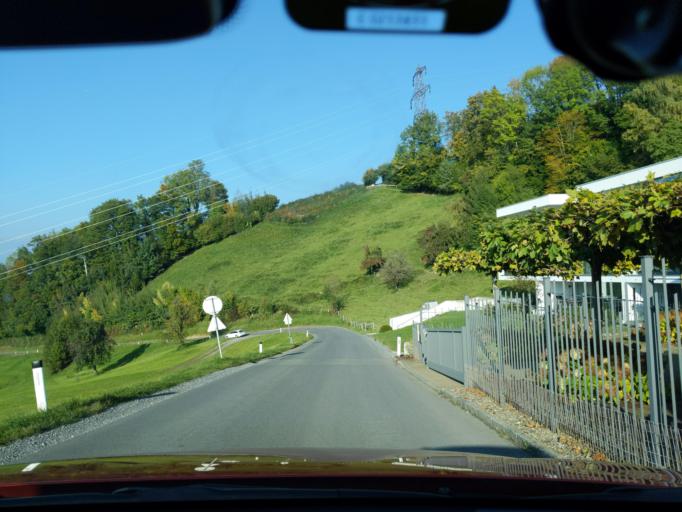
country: AT
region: Vorarlberg
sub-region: Politischer Bezirk Bregenz
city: Bregenz
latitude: 47.5163
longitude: 9.7596
